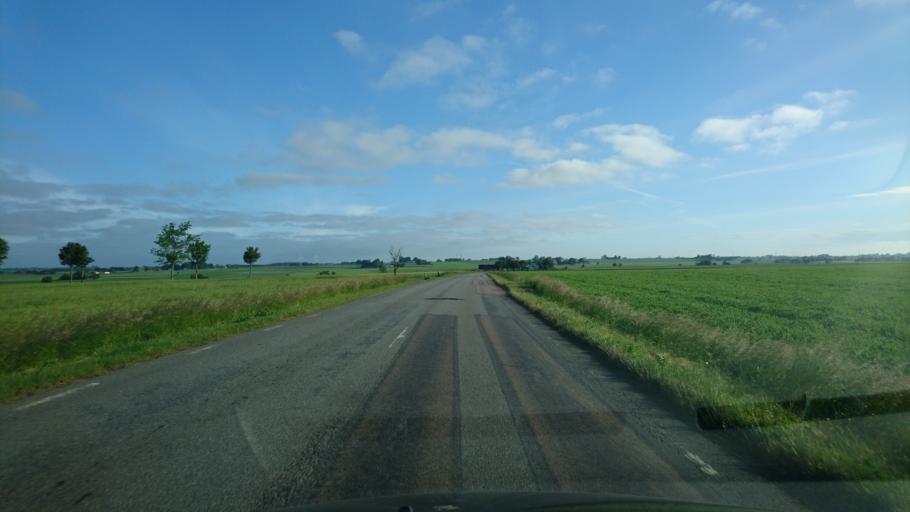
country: SE
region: Skane
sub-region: Tomelilla Kommun
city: Tomelilla
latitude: 55.4661
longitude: 14.0978
